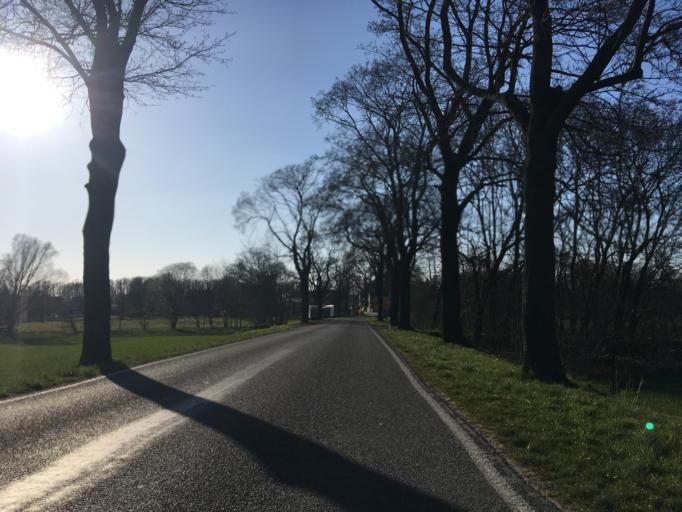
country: DE
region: Berlin
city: Buch
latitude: 52.6246
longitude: 13.5488
